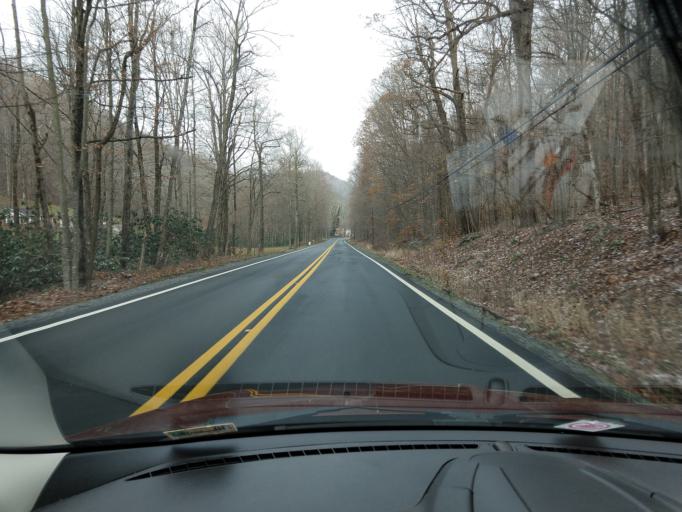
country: US
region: West Virginia
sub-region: Nicholas County
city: Richwood
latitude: 38.1390
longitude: -80.6856
